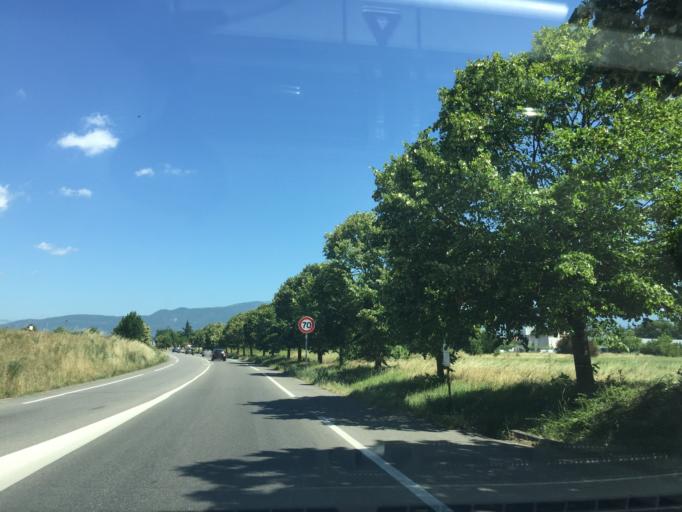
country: FR
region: Rhone-Alpes
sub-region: Departement de la Drome
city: Mours-Saint-Eusebe
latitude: 45.0573
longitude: 5.0650
